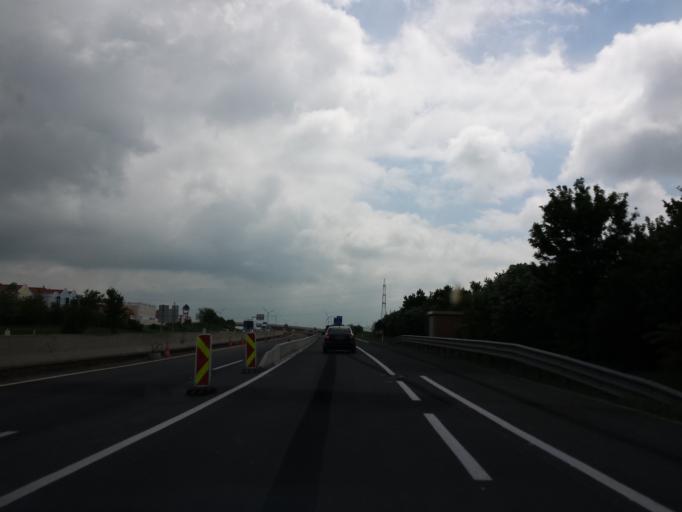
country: AT
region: Burgenland
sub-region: Politischer Bezirk Neusiedl am See
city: Parndorf
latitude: 47.9770
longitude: 16.8454
